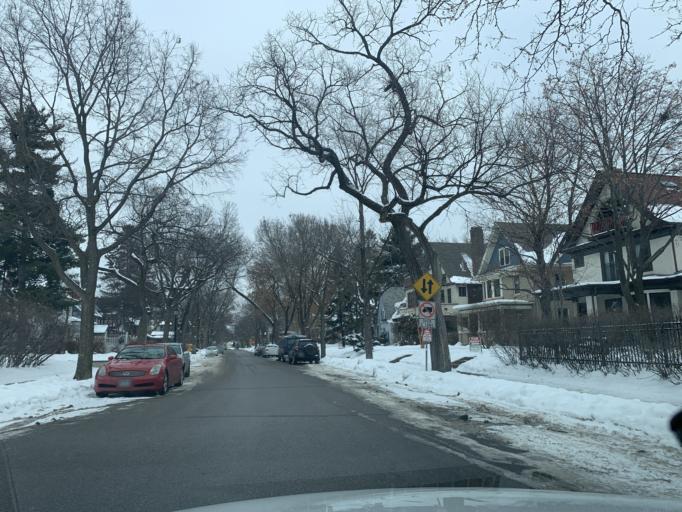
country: US
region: Minnesota
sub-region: Hennepin County
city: Minneapolis
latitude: 44.9527
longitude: -93.3012
